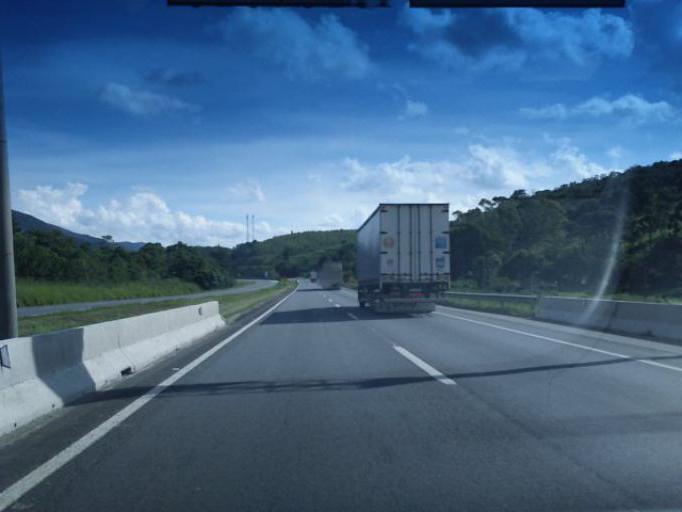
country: BR
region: Parana
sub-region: Campina Grande Do Sul
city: Campina Grande do Sul
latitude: -25.1240
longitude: -48.8565
